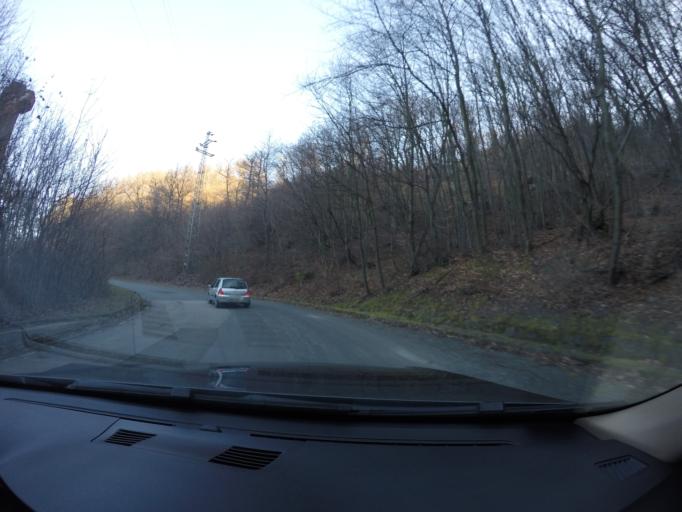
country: HU
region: Pest
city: Visegrad
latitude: 47.7964
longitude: 18.9853
